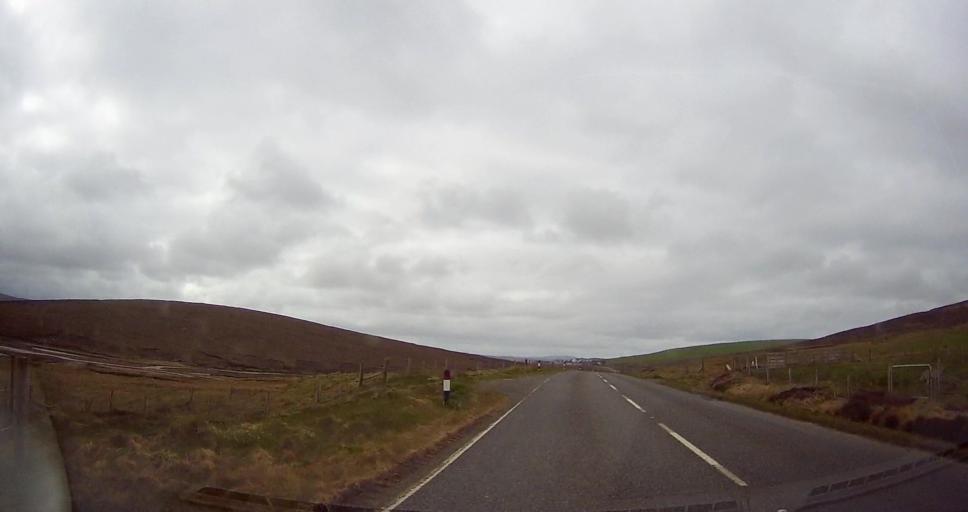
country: GB
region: Scotland
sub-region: Shetland Islands
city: Lerwick
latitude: 60.2502
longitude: -1.3777
